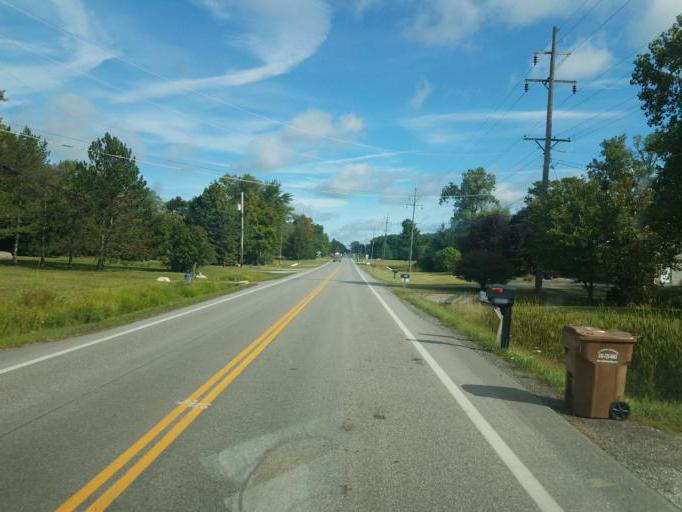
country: US
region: Ohio
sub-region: Wayne County
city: West Salem
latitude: 41.0862
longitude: -82.1236
